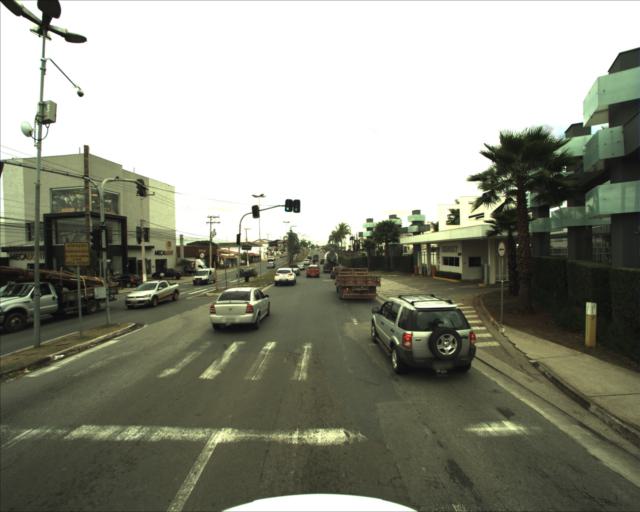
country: BR
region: Sao Paulo
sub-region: Votorantim
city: Votorantim
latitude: -23.5418
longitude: -47.4666
